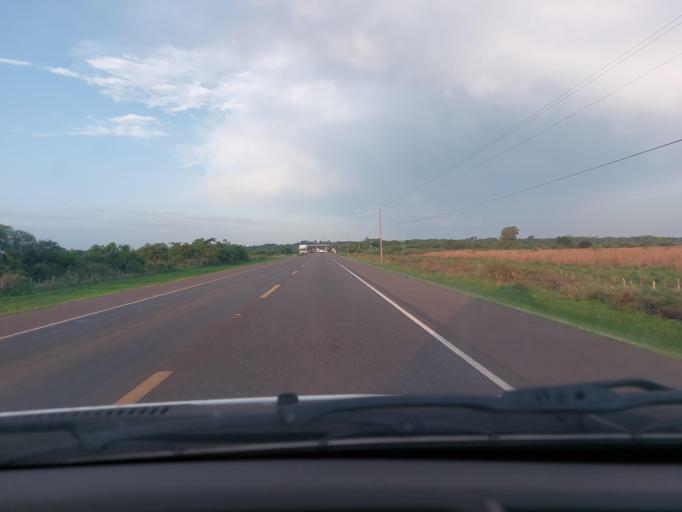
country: PY
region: San Pedro
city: Union
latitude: -24.8193
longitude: -56.7463
